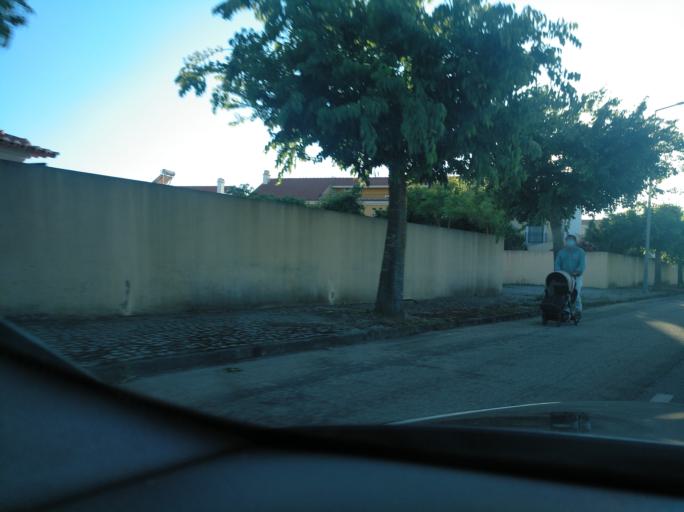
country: PT
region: Portalegre
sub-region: Elvas
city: Elvas
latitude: 38.8760
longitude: -7.1906
